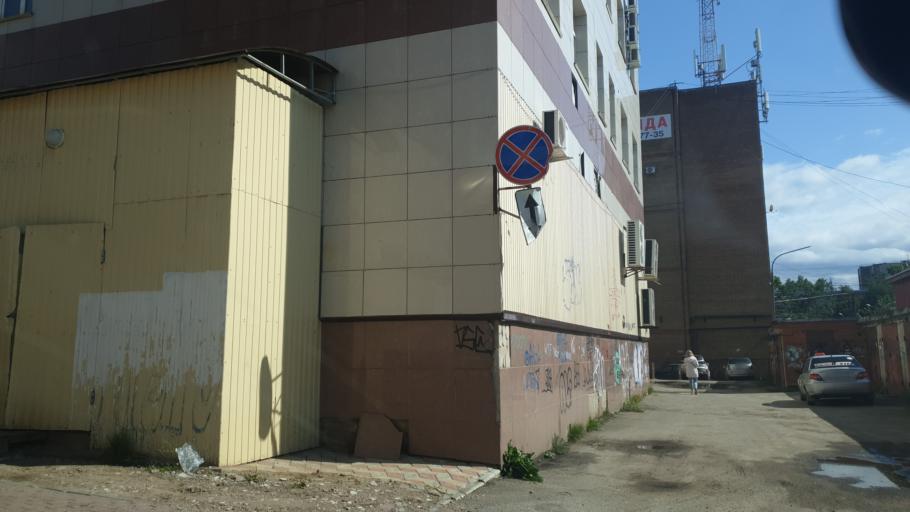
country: RU
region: Komi Republic
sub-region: Syktyvdinskiy Rayon
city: Syktyvkar
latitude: 61.6635
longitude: 50.8328
